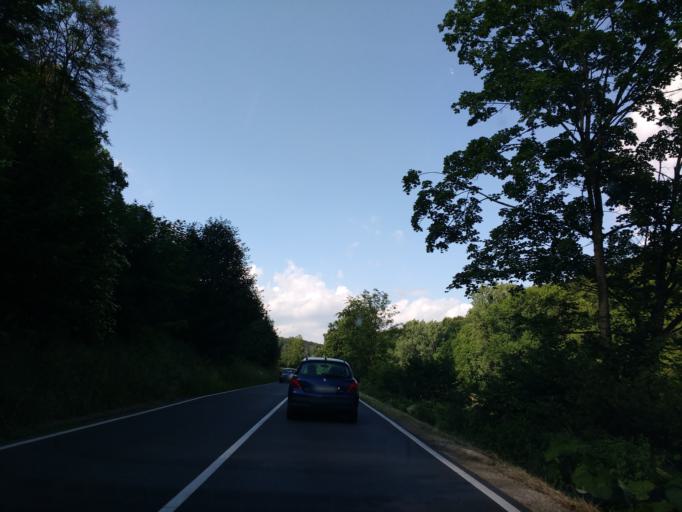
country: DE
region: North Rhine-Westphalia
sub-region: Regierungsbezirk Detmold
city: Vlotho
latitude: 52.1387
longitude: 8.9484
